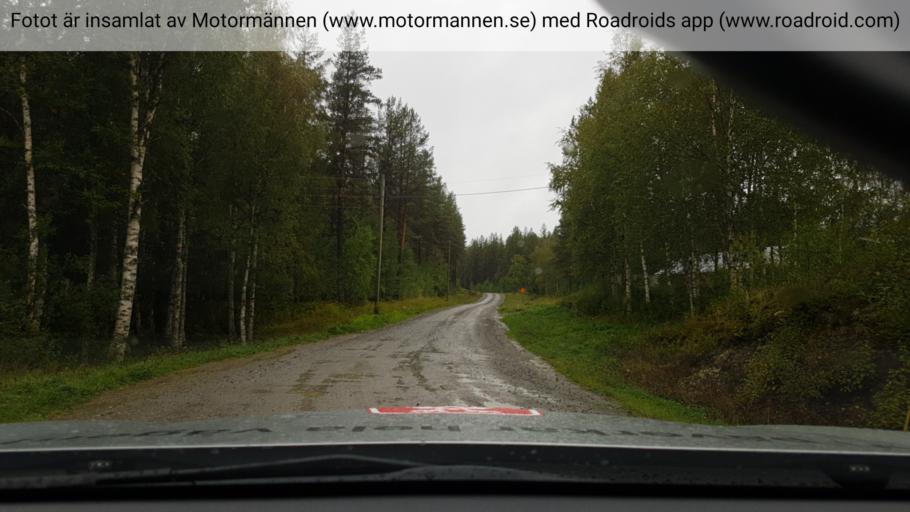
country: SE
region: Vaesterbotten
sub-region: Asele Kommun
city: Asele
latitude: 64.0771
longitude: 17.5755
